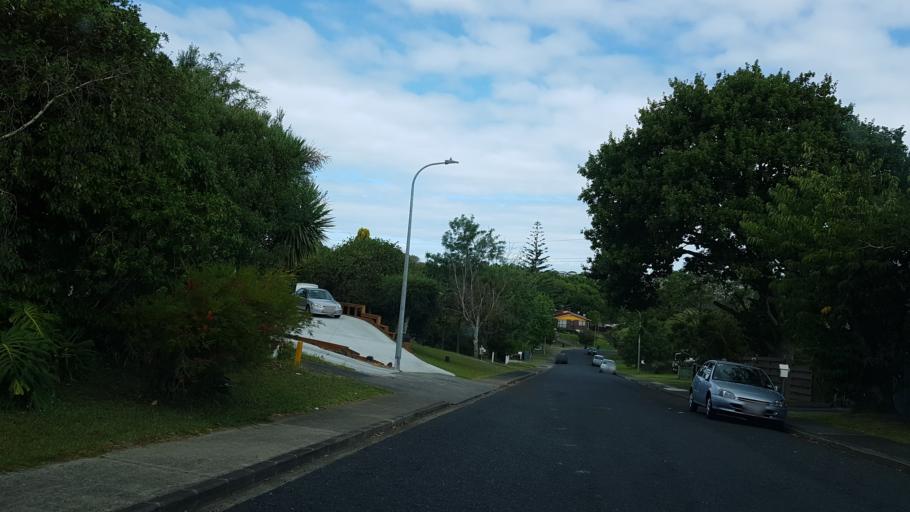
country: NZ
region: Auckland
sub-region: Auckland
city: North Shore
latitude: -36.7809
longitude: 174.7306
